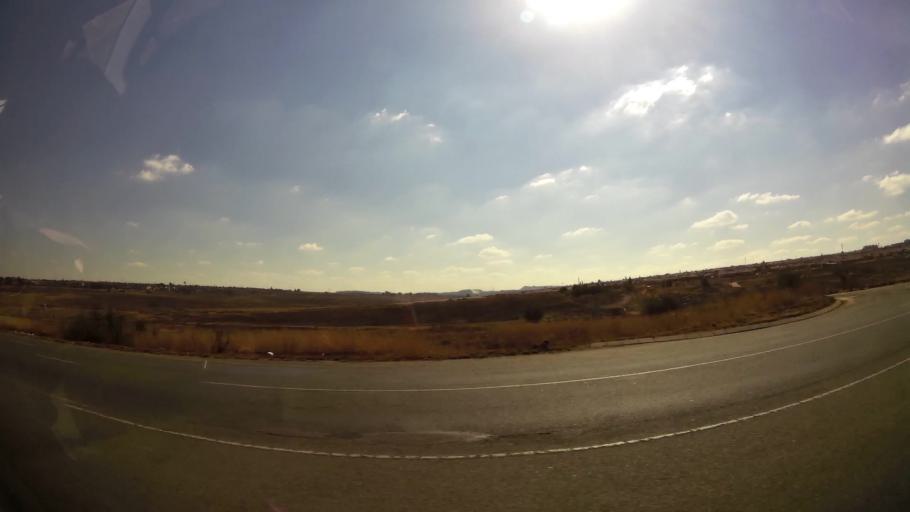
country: ZA
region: Gauteng
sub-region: West Rand District Municipality
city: Randfontein
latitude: -26.1759
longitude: 27.7725
